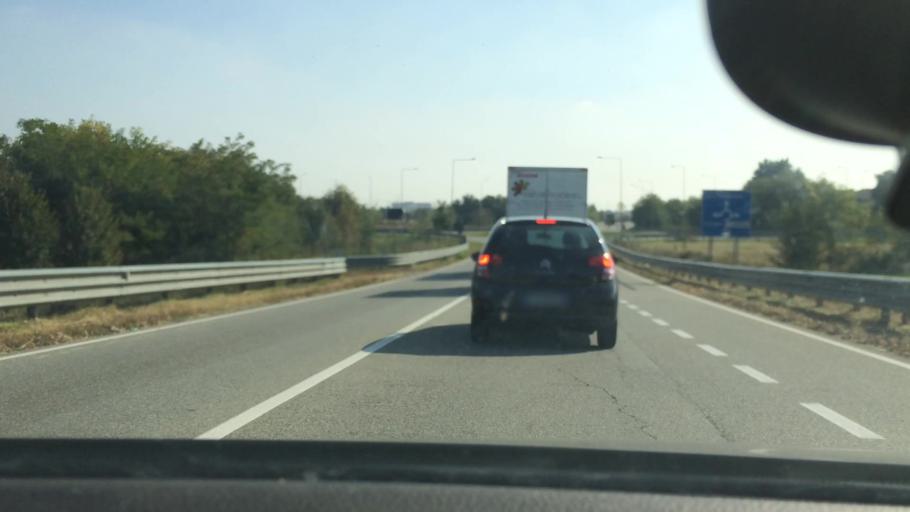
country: IT
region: Lombardy
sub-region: Citta metropolitana di Milano
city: Casone
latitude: 45.4894
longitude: 8.8805
